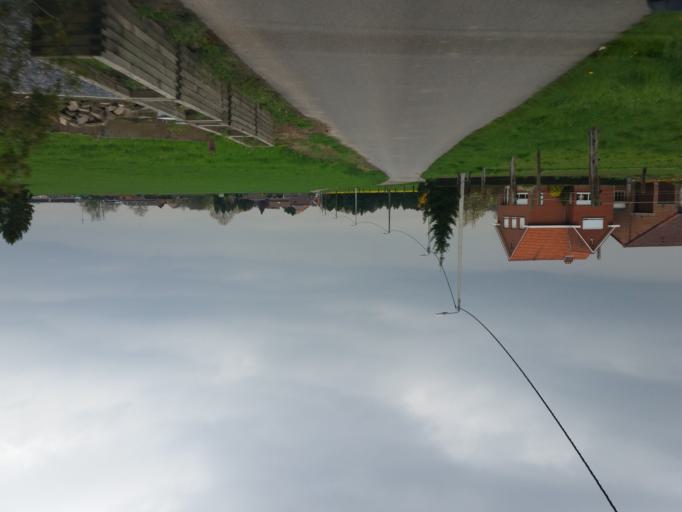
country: BE
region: Flanders
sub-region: Provincie Vlaams-Brabant
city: Steenokkerzeel
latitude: 50.9247
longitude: 4.5305
